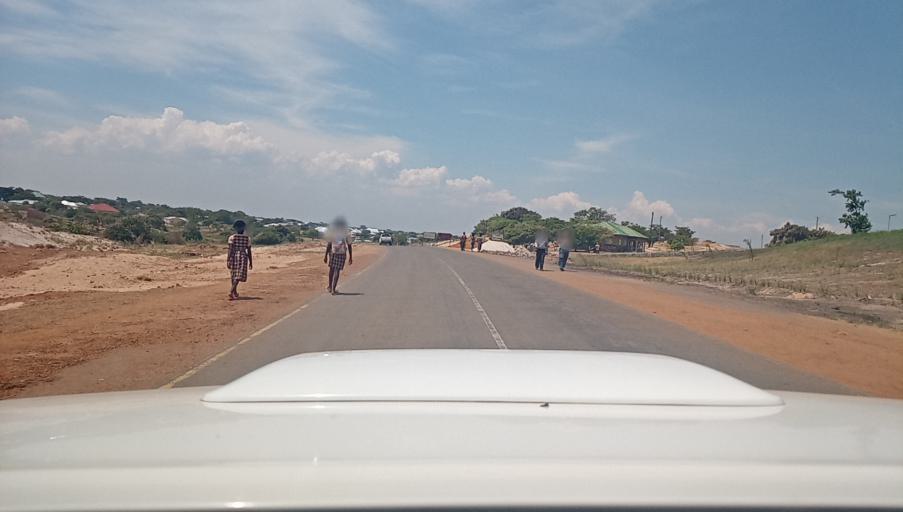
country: ZM
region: Luapula
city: Samfya
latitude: -11.3498
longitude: 29.5580
